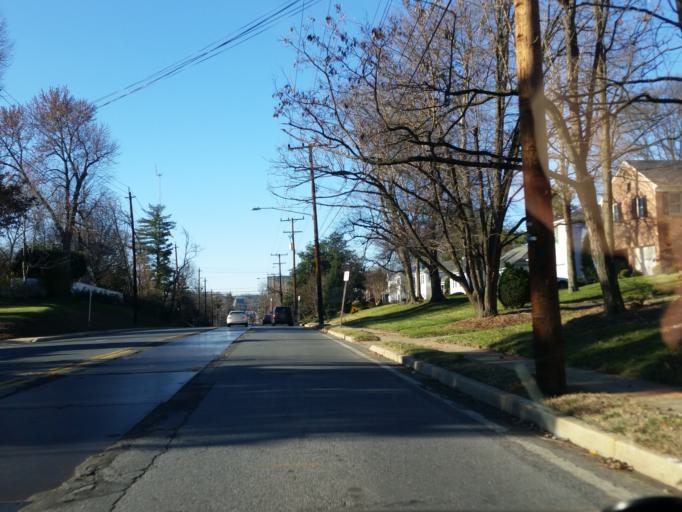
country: US
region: Maryland
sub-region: Montgomery County
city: Friendship Village
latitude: 38.9579
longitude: -77.0931
